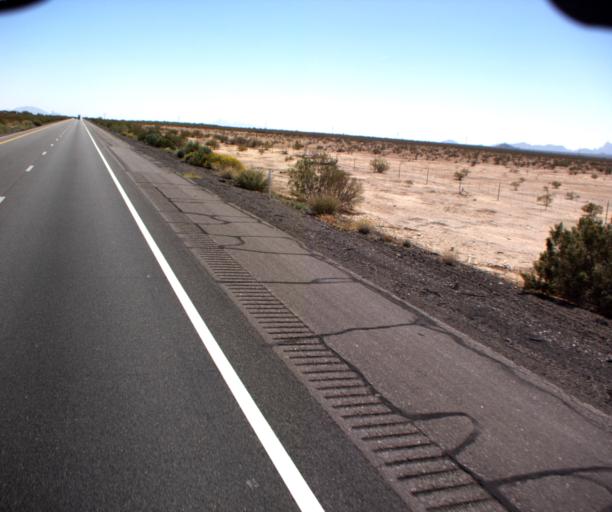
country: US
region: Arizona
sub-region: La Paz County
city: Salome
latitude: 33.5822
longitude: -113.4422
